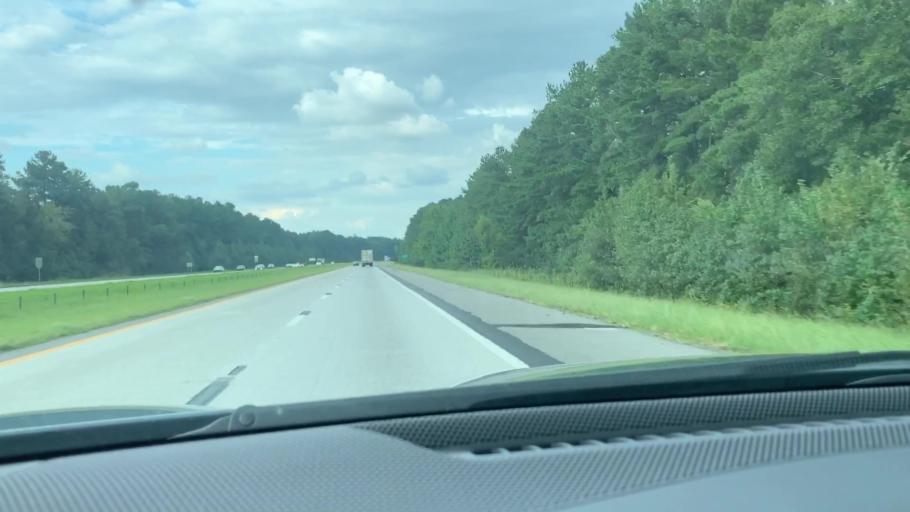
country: US
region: South Carolina
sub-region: Dorchester County
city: Saint George
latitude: 33.3045
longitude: -80.5549
